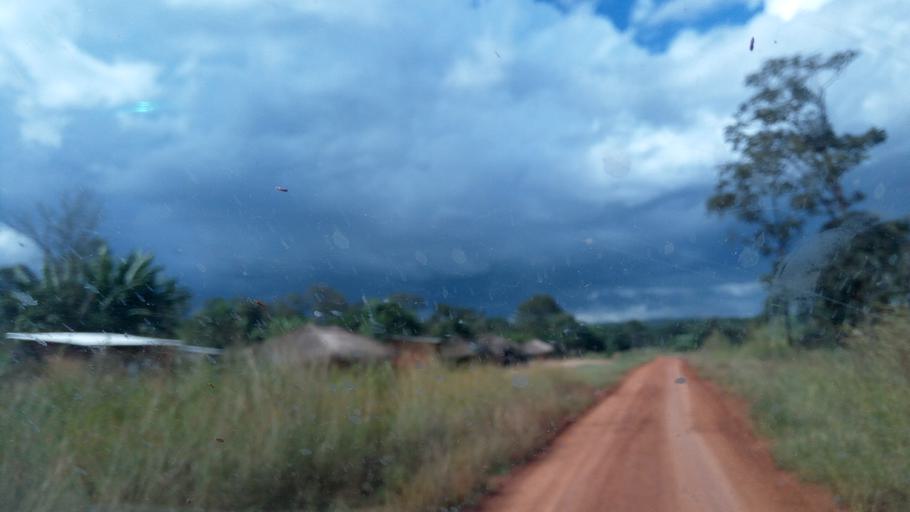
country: ZM
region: Northern
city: Kaputa
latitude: -8.1297
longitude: 29.1248
